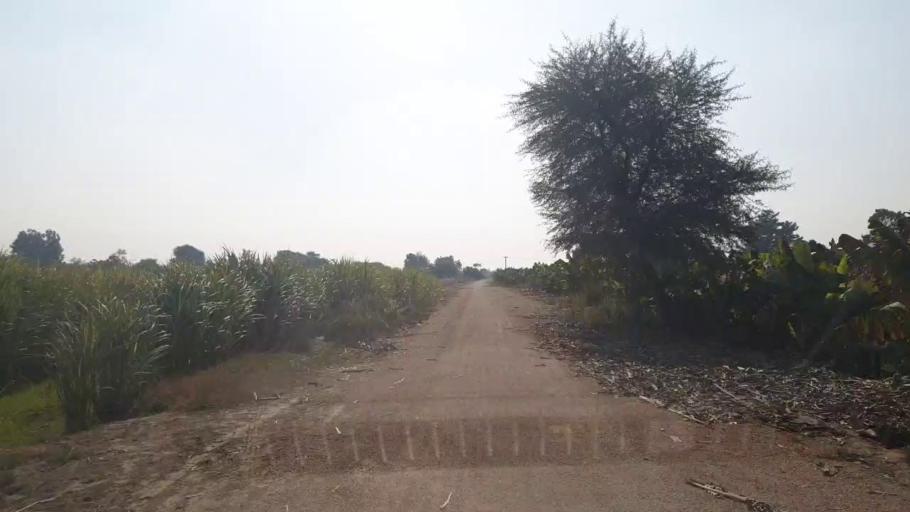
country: PK
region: Sindh
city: Shahdadpur
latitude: 25.9694
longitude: 68.5403
